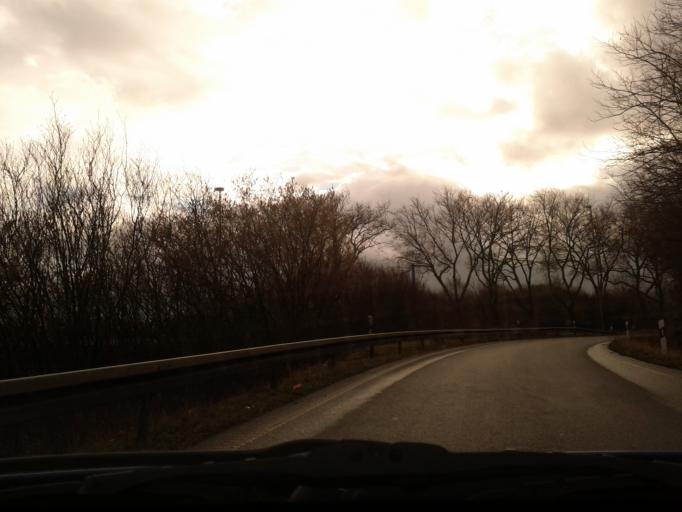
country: DE
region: North Rhine-Westphalia
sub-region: Regierungsbezirk Arnsberg
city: Dortmund
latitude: 51.5059
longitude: 7.5211
